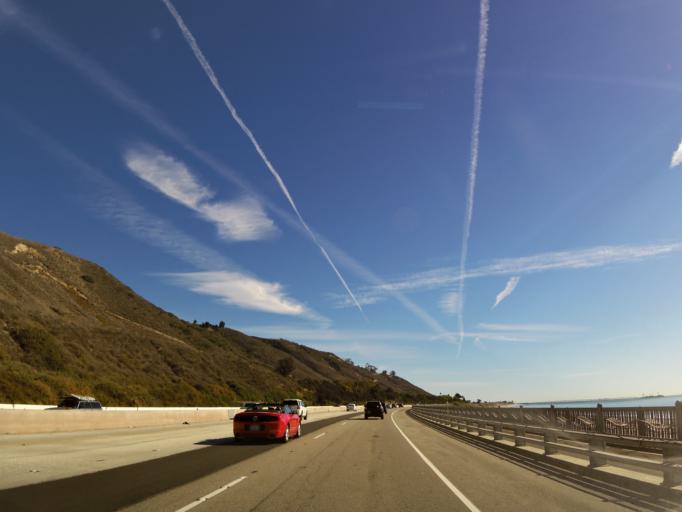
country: US
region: California
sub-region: Santa Barbara County
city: Carpinteria
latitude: 34.3734
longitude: -119.4590
